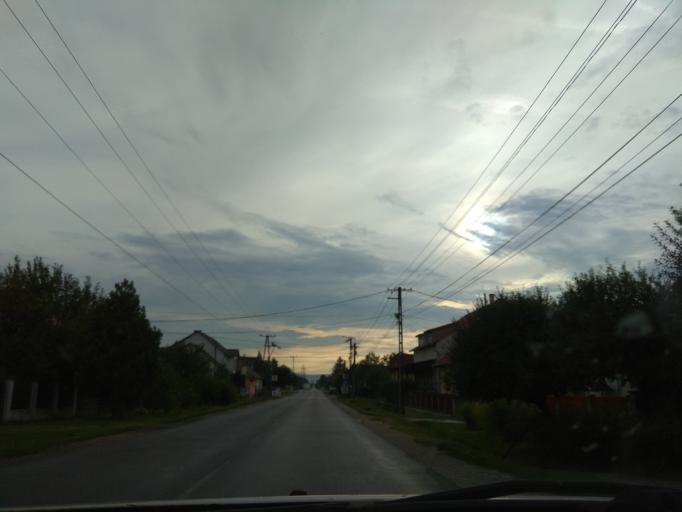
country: HU
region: Borsod-Abauj-Zemplen
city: Onga
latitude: 48.1204
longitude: 20.9109
